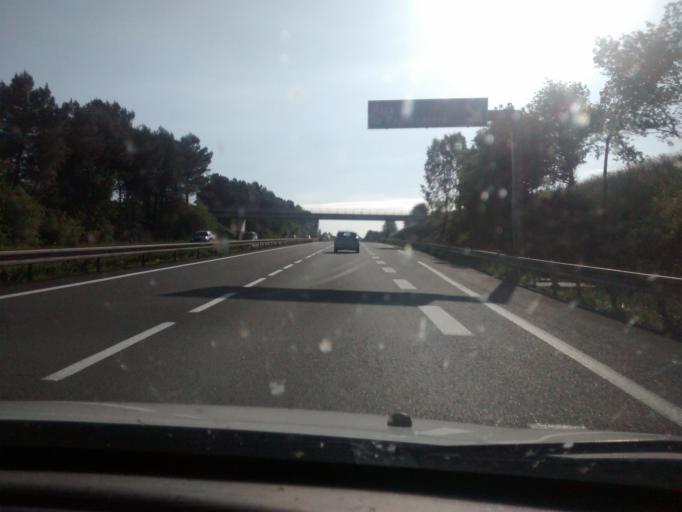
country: FR
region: Pays de la Loire
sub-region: Departement de la Mayenne
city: Loiron
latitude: 48.0772
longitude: -0.9140
